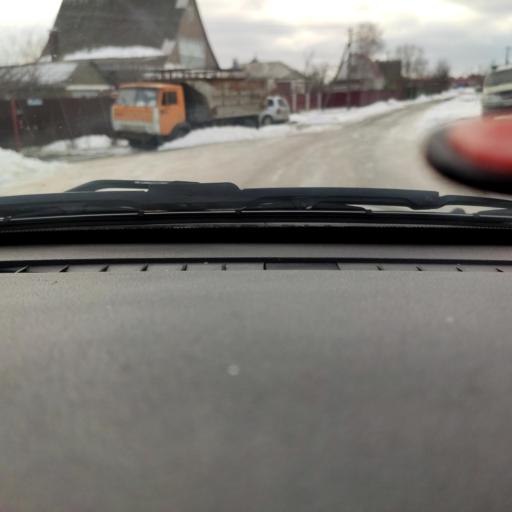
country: RU
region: Voronezj
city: Semiluki
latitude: 51.7160
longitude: 39.0351
